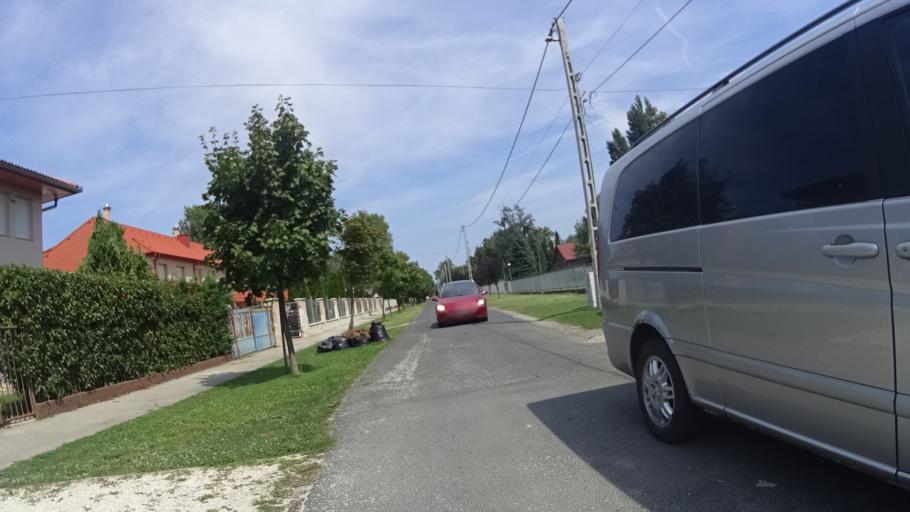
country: HU
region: Somogy
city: Balatonboglar
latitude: 46.7688
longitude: 17.6220
